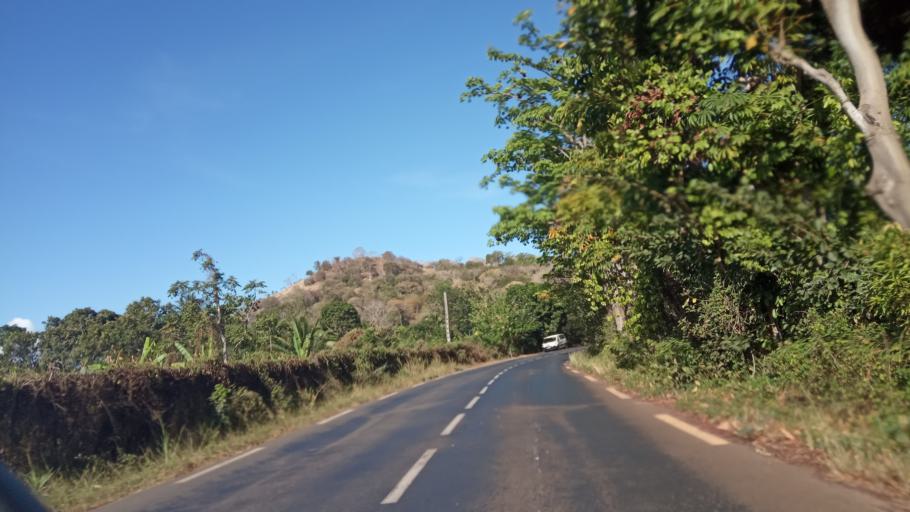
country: YT
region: Dembeni
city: Dembeni
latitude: -12.8685
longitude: 45.2020
